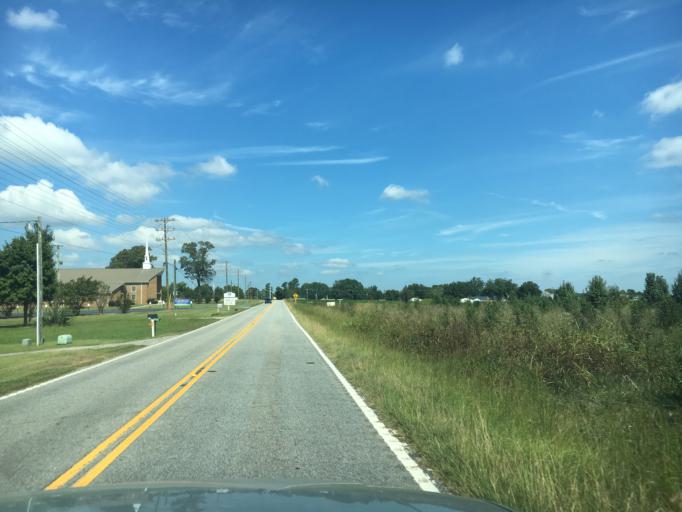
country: US
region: South Carolina
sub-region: Spartanburg County
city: Boiling Springs
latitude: 35.0825
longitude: -81.9287
